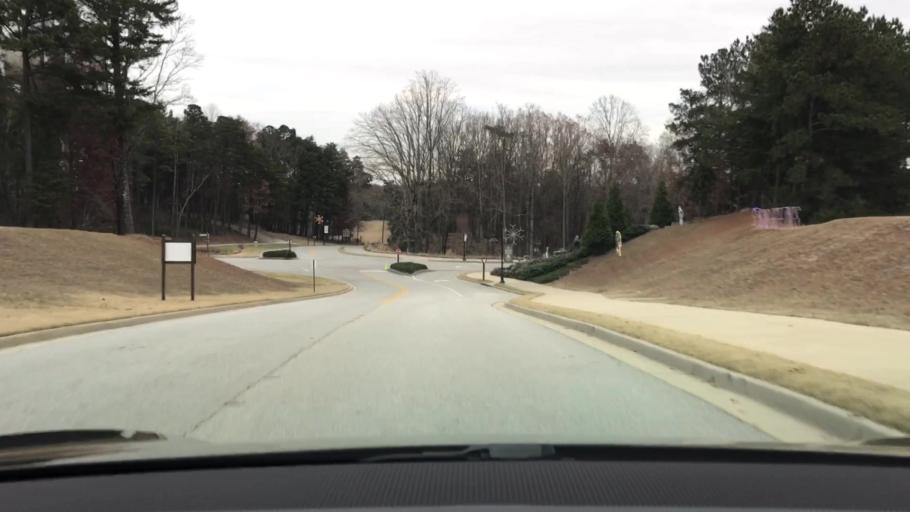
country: US
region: Georgia
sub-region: Gwinnett County
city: Buford
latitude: 34.1766
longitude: -84.0267
